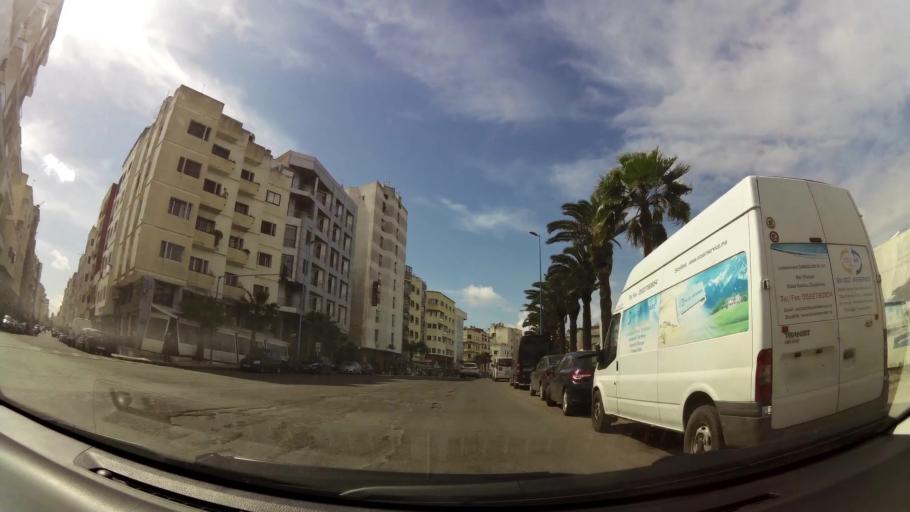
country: MA
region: Grand Casablanca
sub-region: Casablanca
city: Casablanca
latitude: 33.5856
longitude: -7.6394
